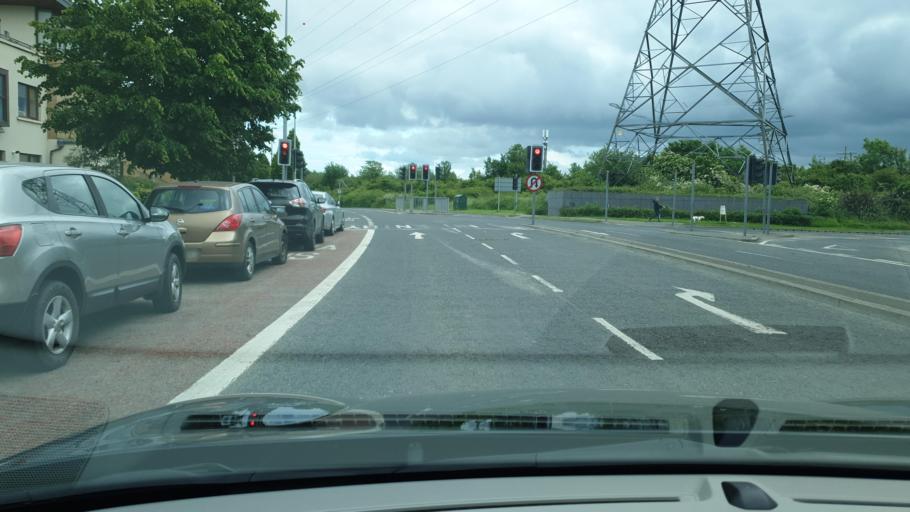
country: IE
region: Leinster
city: Lucan
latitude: 53.3364
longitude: -6.4575
